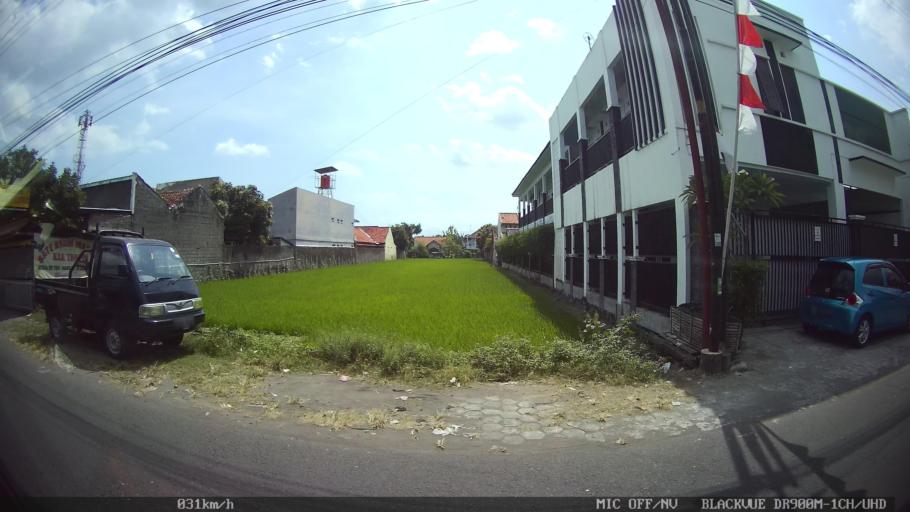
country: ID
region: Daerah Istimewa Yogyakarta
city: Gamping Lor
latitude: -7.8077
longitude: 110.3393
